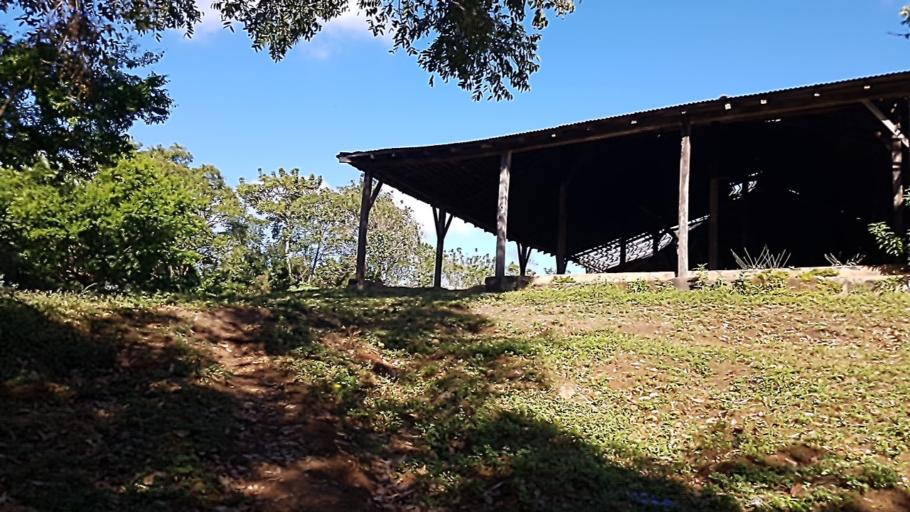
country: NI
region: Carazo
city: La Paz de Oriente
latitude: 11.8255
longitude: -86.1328
